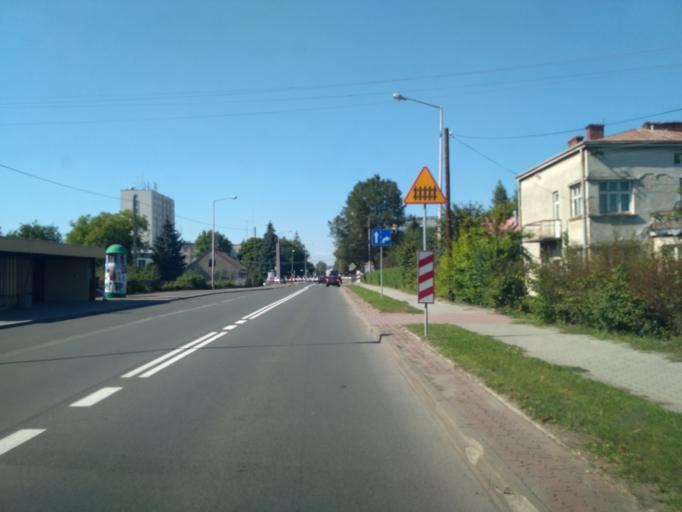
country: PL
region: Subcarpathian Voivodeship
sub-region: Krosno
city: Krosno
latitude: 49.6818
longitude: 21.7723
